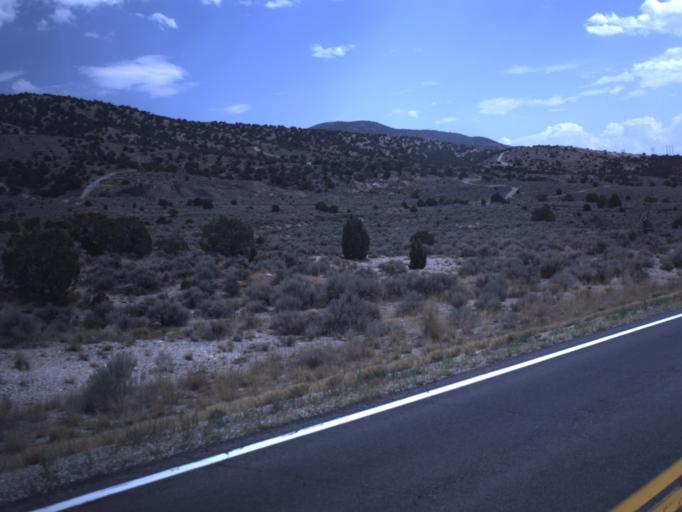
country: US
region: Utah
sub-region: Tooele County
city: Tooele
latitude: 40.3264
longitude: -112.2895
